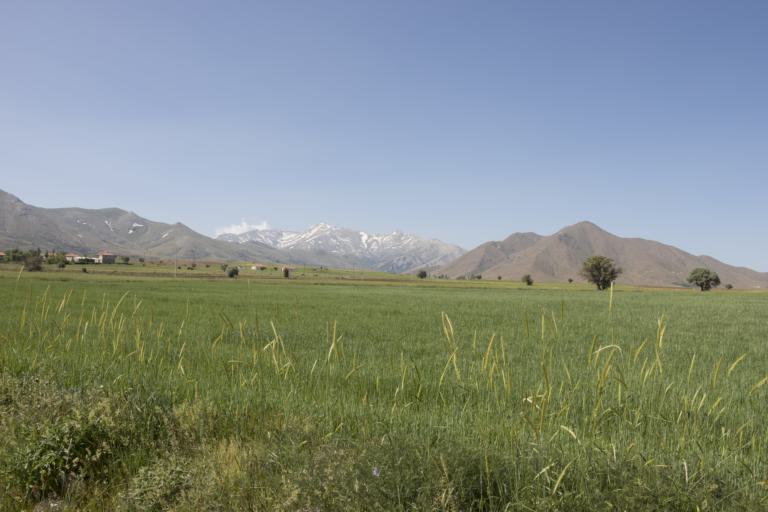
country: TR
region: Kayseri
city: Toklar
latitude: 38.4269
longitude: 36.0899
